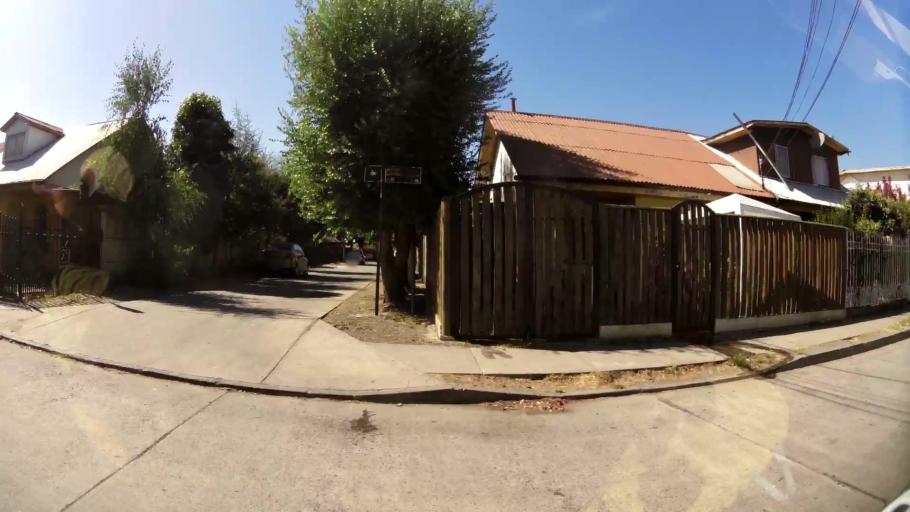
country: CL
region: Maule
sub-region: Provincia de Curico
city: Curico
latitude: -34.9726
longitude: -71.2592
